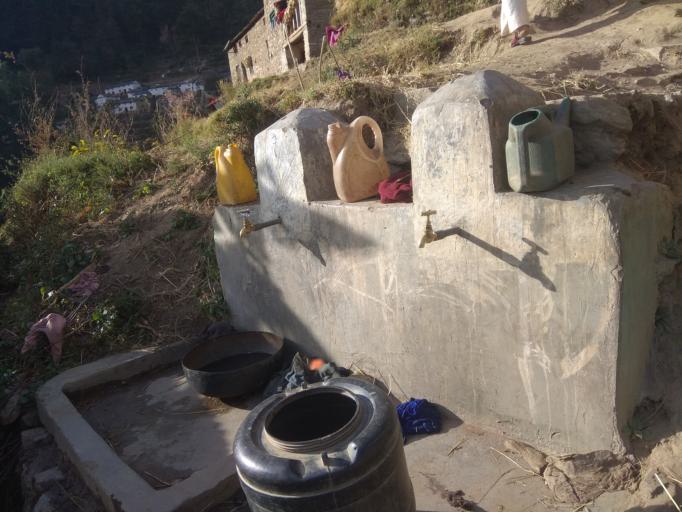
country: NP
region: Mid Western
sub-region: Bheri Zone
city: Dailekh
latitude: 29.2513
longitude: 81.6626
